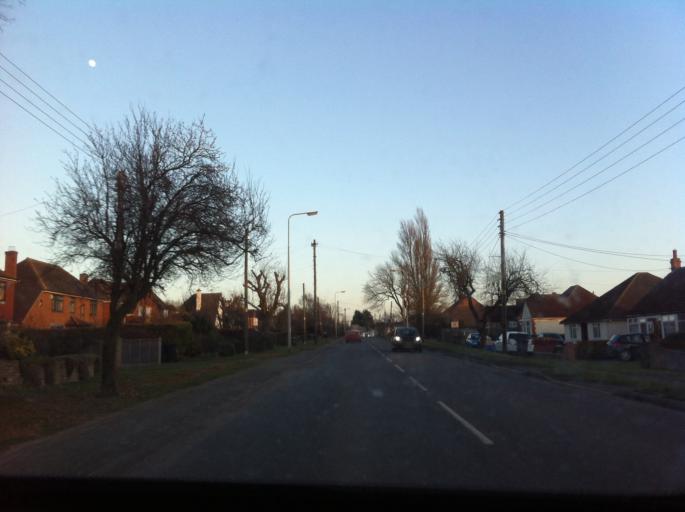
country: GB
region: England
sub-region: Northamptonshire
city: Irchester
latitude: 52.2805
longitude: -0.6581
